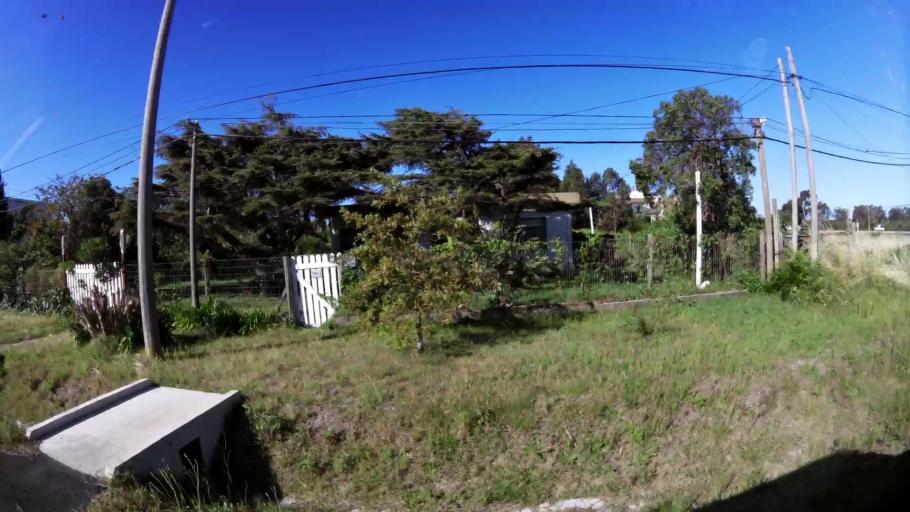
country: UY
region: Canelones
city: Barra de Carrasco
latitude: -34.8723
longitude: -56.0193
